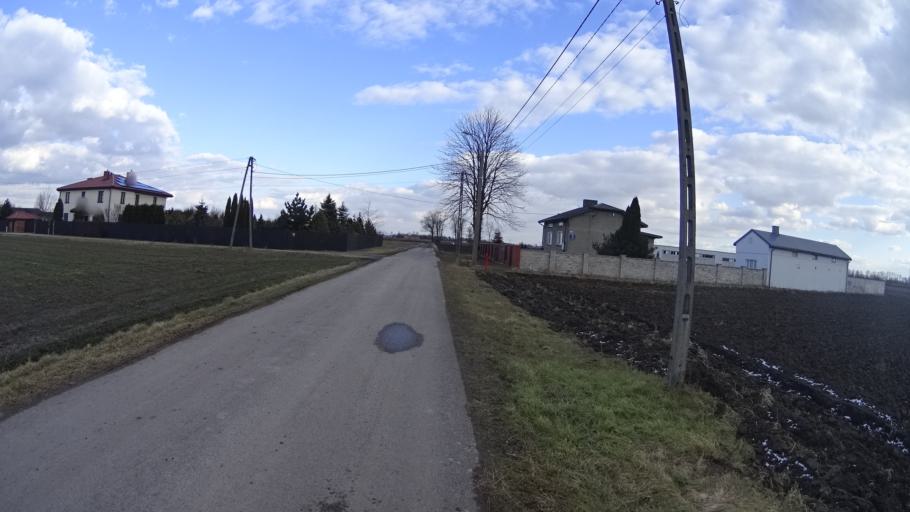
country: PL
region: Masovian Voivodeship
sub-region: Powiat warszawski zachodni
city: Ozarow Mazowiecki
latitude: 52.2454
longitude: 20.7920
